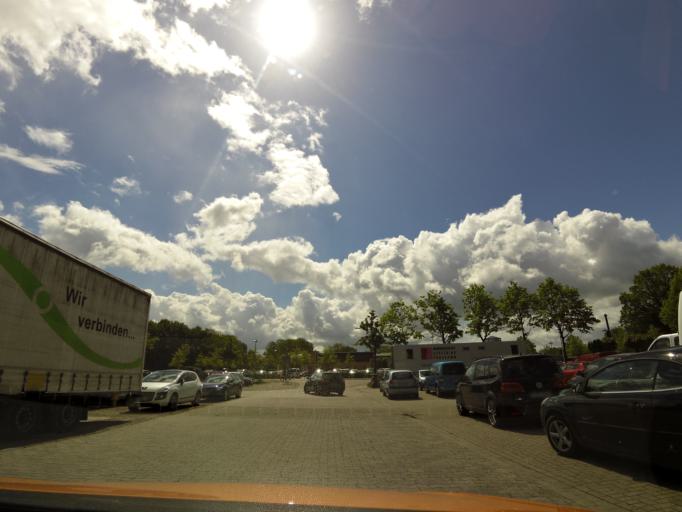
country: DE
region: Lower Saxony
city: Delmenhorst
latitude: 53.0470
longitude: 8.6208
